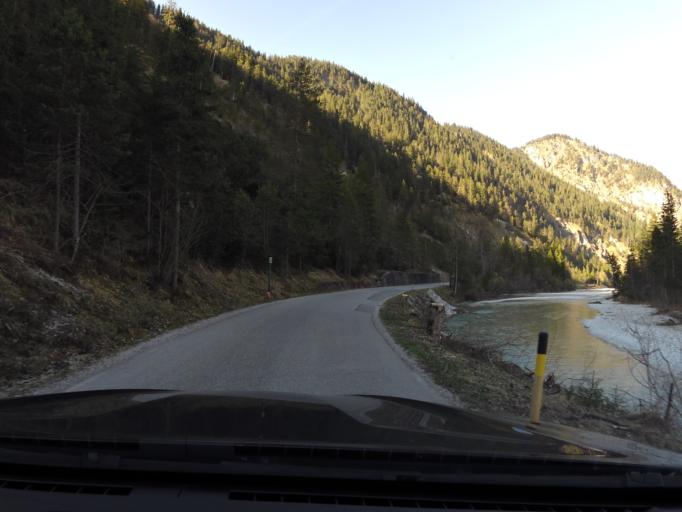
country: DE
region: Bavaria
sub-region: Upper Bavaria
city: Jachenau
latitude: 47.5560
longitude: 11.4286
